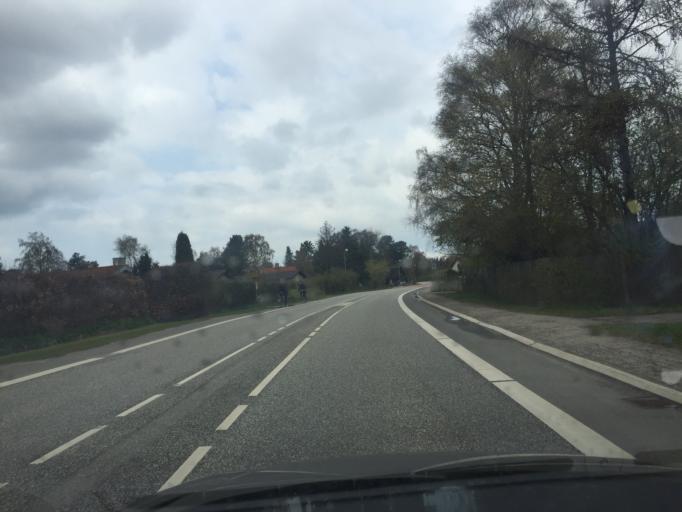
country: DK
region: Capital Region
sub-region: Halsnaes Kommune
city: Frederiksvaerk
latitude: 56.0012
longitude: 12.0129
